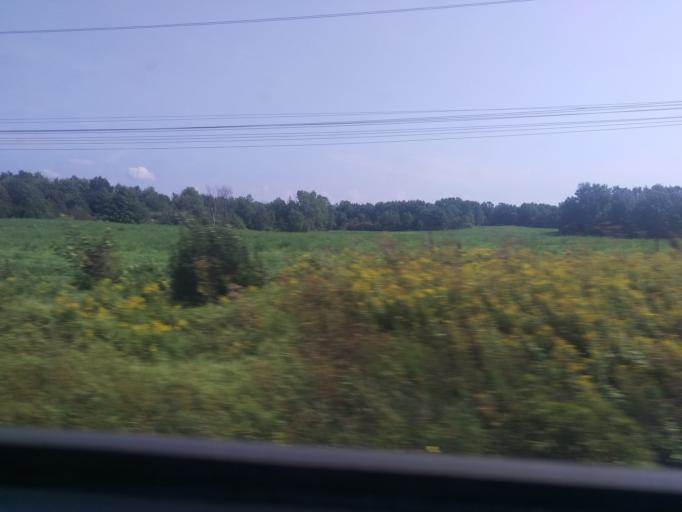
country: US
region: New York
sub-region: Jefferson County
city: Alexandria Bay
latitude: 44.4572
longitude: -75.9203
